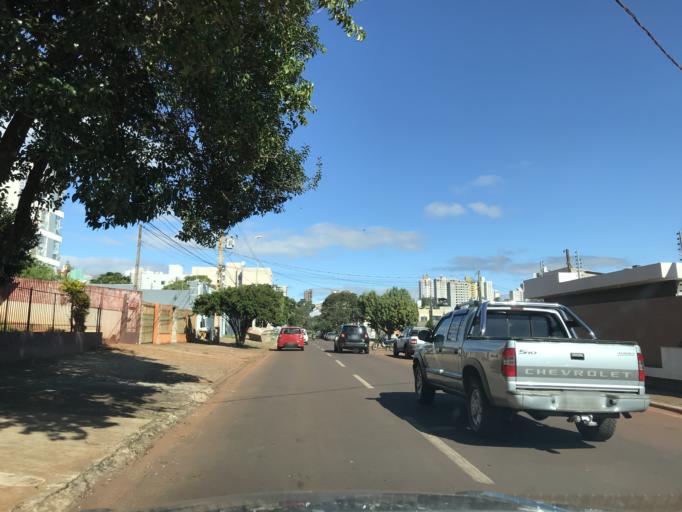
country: BR
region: Parana
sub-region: Cascavel
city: Cascavel
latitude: -24.9436
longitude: -53.4686
